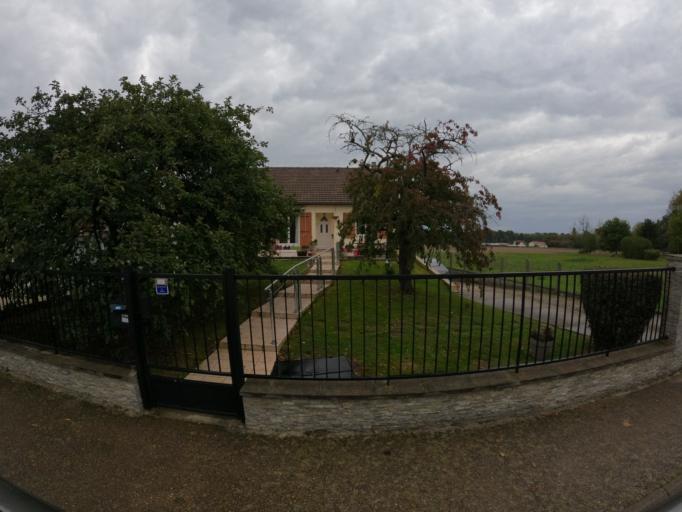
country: FR
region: Ile-de-France
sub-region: Departement de Seine-et-Marne
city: Villeneuve-le-Comte
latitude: 48.8127
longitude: 2.8330
